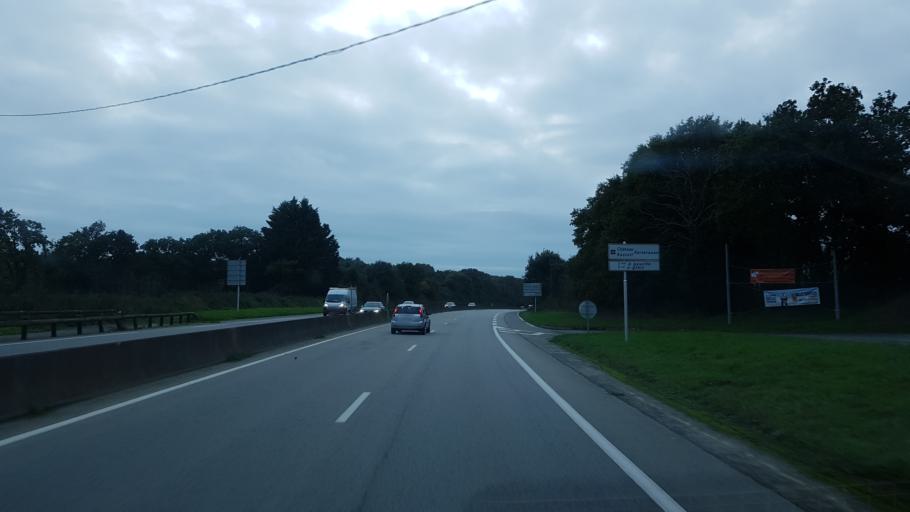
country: FR
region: Brittany
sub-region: Departement du Morbihan
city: Sarzeau
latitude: 47.5445
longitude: -2.7228
